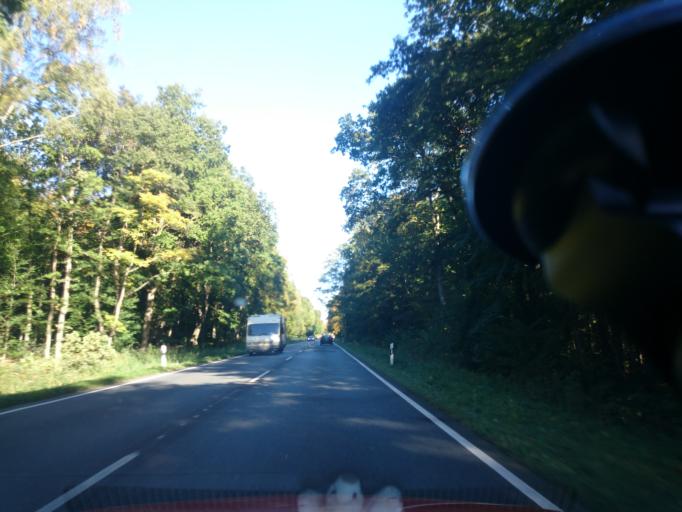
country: DE
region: Mecklenburg-Vorpommern
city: Gelbensande
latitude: 54.2174
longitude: 12.3519
